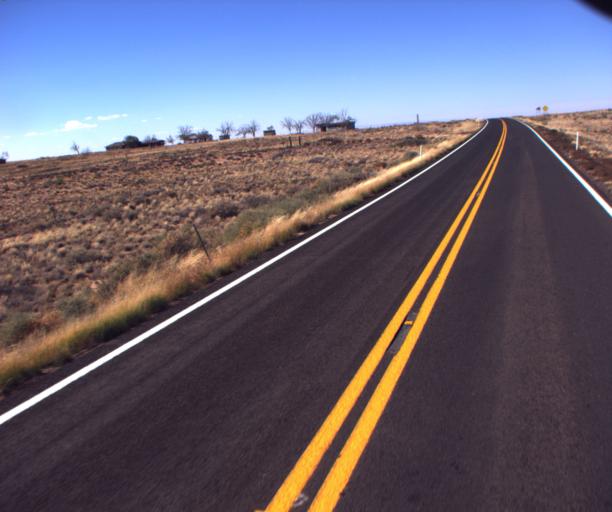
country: US
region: Arizona
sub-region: Coconino County
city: Tuba City
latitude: 35.9595
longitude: -110.9361
